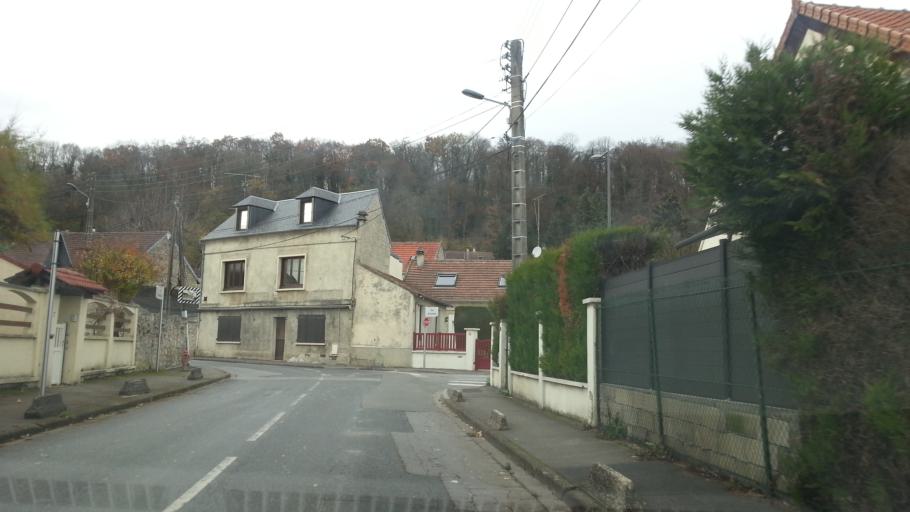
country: FR
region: Picardie
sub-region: Departement de l'Oise
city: Montataire
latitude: 49.2620
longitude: 2.4516
